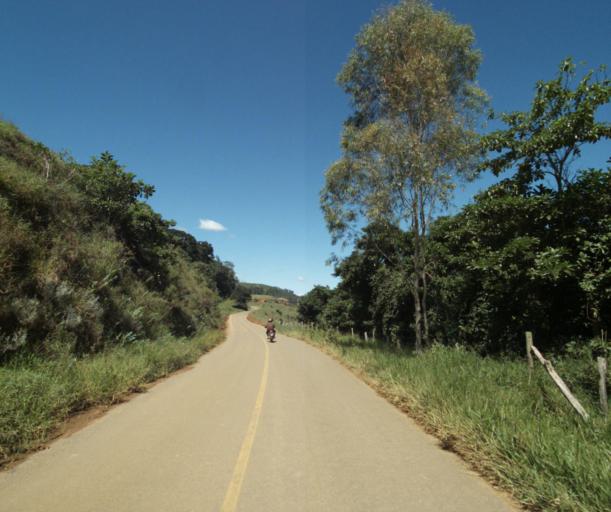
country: BR
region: Minas Gerais
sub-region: Espera Feliz
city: Espera Feliz
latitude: -20.5794
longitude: -41.8362
